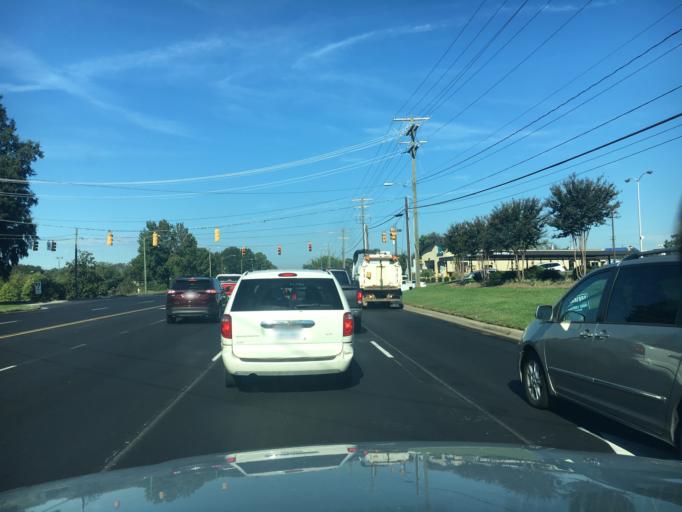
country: US
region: North Carolina
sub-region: Catawba County
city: Hickory
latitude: 35.7053
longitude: -81.3017
